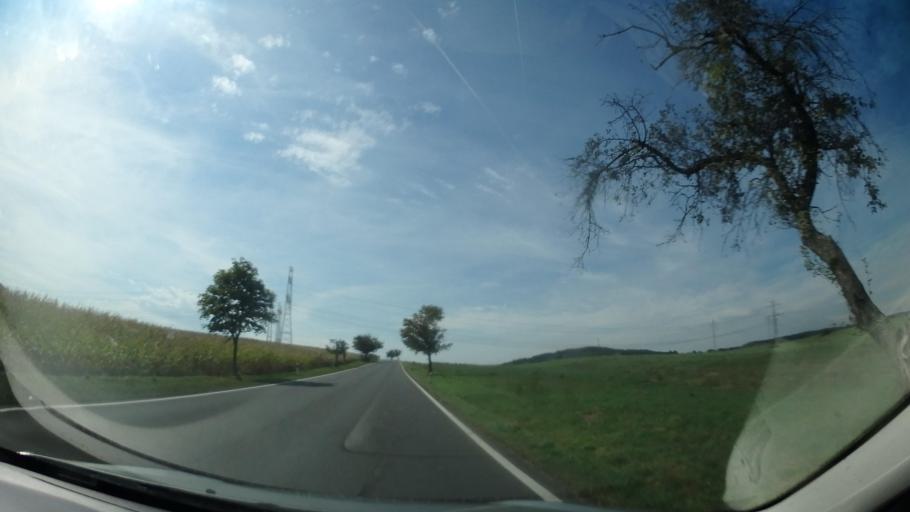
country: CZ
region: Jihocesky
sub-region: Okres Pisek
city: Pisek
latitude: 49.3072
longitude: 14.0895
